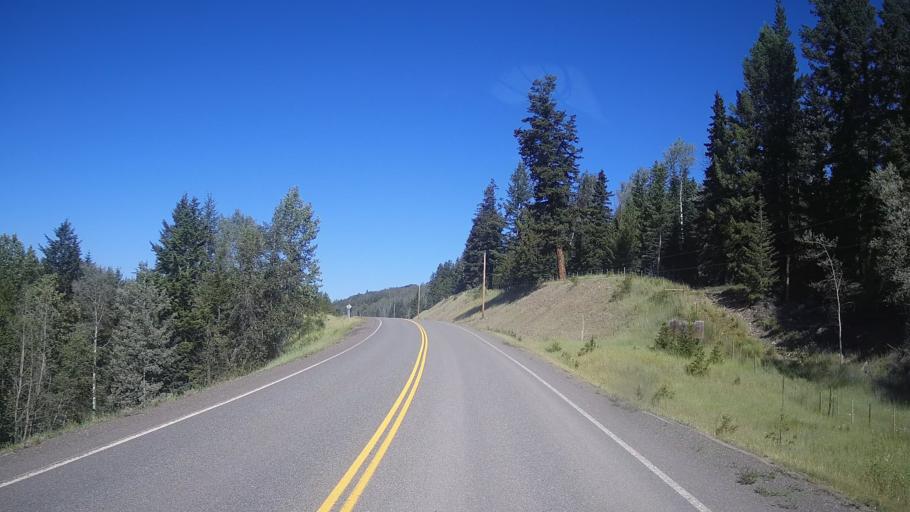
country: CA
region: British Columbia
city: Kamloops
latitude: 51.4928
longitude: -120.5696
